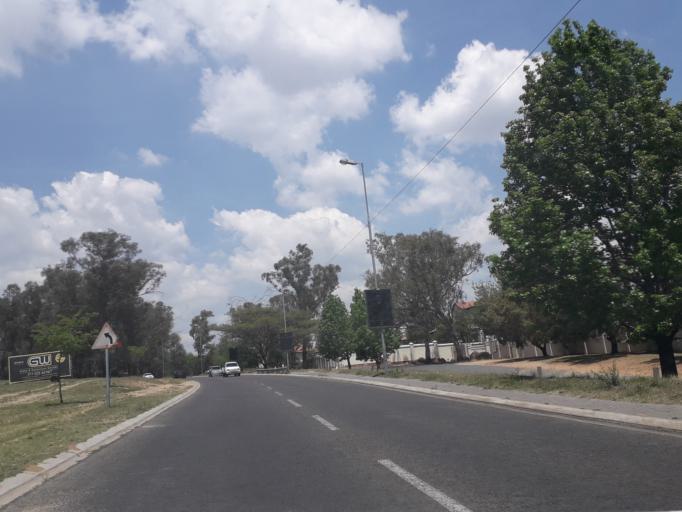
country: ZA
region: Gauteng
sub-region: City of Johannesburg Metropolitan Municipality
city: Midrand
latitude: -26.0437
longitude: 28.0697
